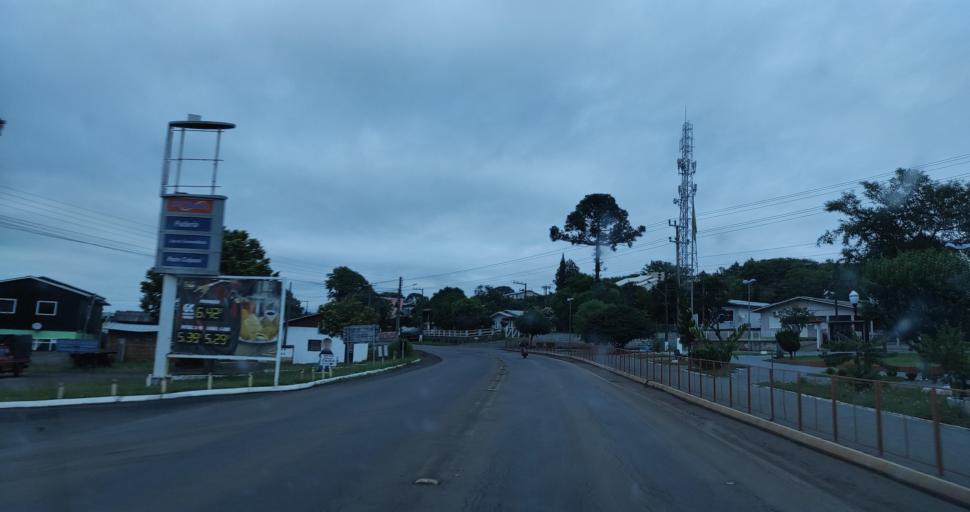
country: BR
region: Santa Catarina
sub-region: Xanxere
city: Xanxere
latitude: -26.7359
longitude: -52.3921
